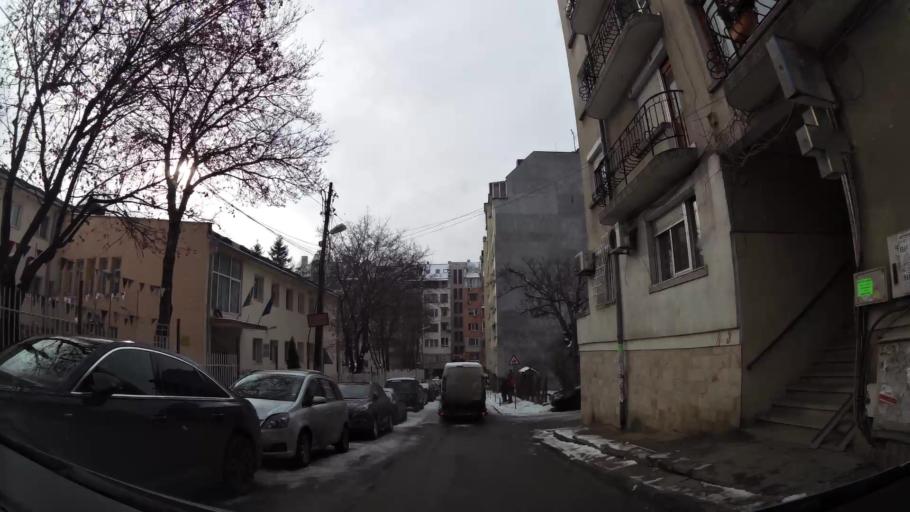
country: BG
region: Sofia-Capital
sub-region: Stolichna Obshtina
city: Sofia
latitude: 42.7076
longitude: 23.3063
